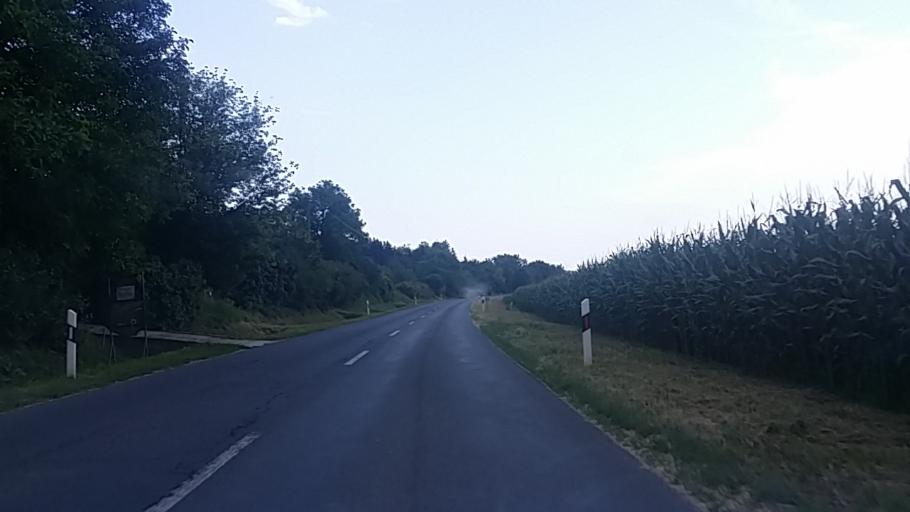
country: HU
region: Zala
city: Cserszegtomaj
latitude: 46.8254
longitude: 17.2005
